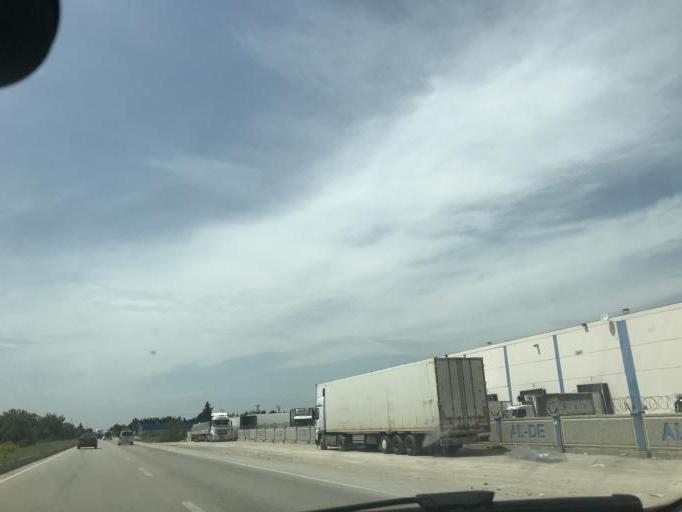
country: TR
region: Adana
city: Yakapinar
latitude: 36.9707
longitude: 35.5272
